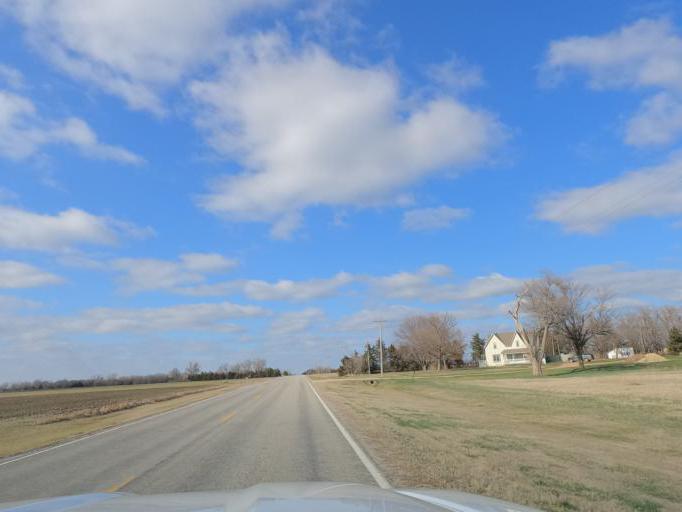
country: US
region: Kansas
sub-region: McPherson County
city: Inman
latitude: 38.2093
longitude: -97.8484
